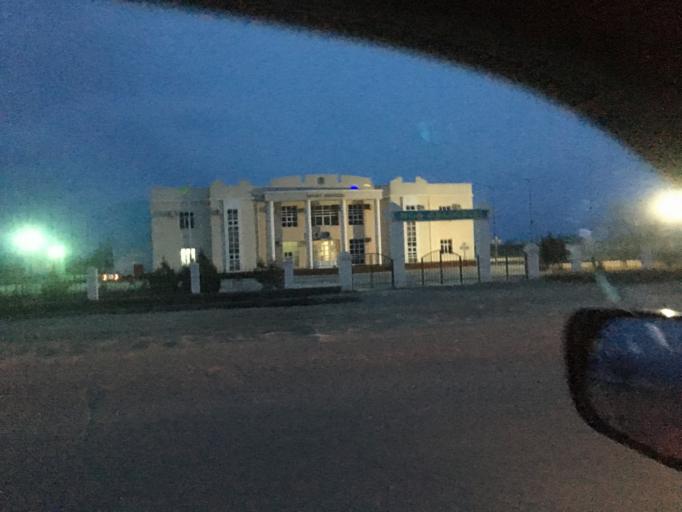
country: TM
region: Dasoguz
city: Yylanly
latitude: 41.8870
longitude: 59.6210
